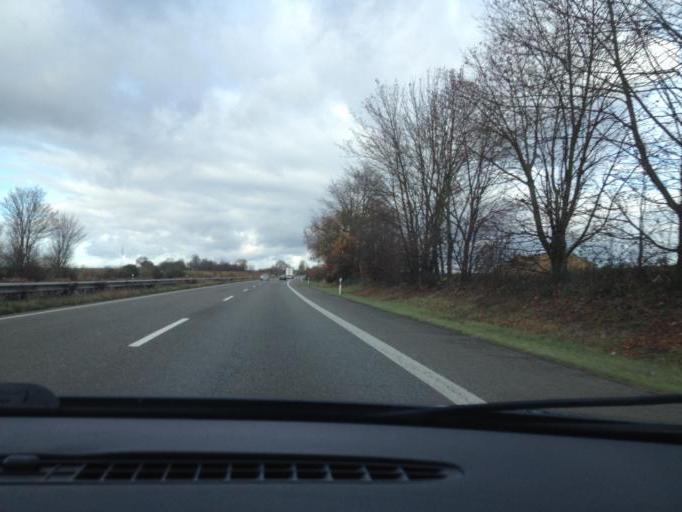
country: DE
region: Rheinland-Pfalz
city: Lingenfeld
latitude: 49.2525
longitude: 8.3317
